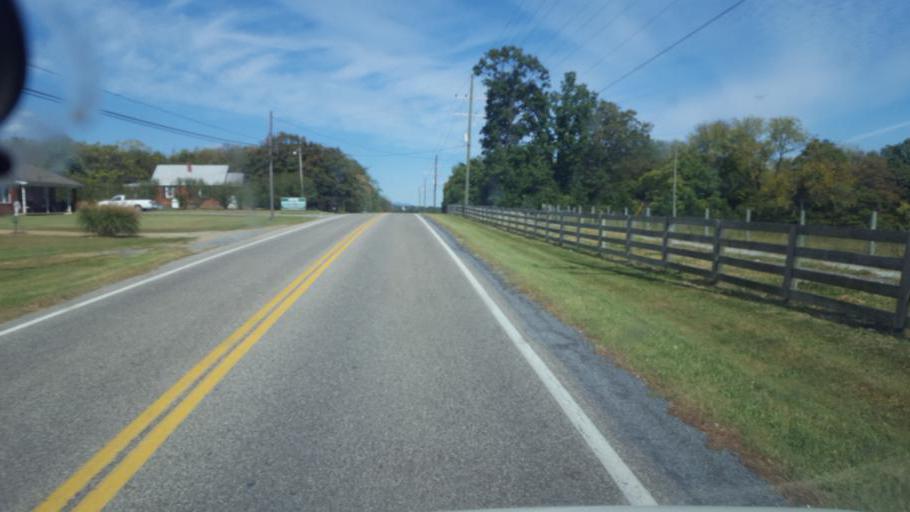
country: US
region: Virginia
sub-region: Page County
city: Shenandoah
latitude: 38.5681
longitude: -78.5986
